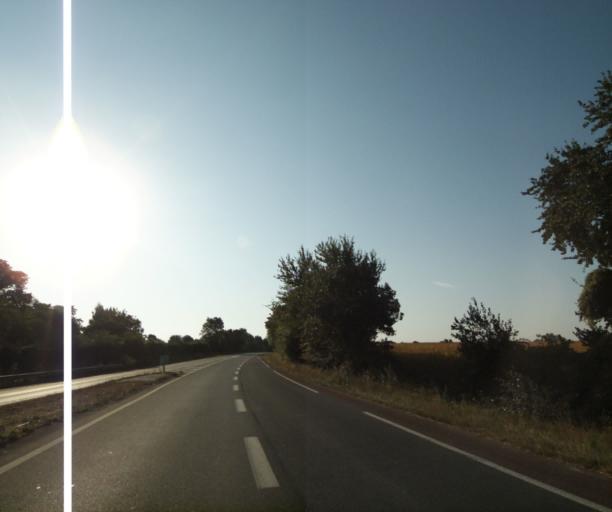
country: FR
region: Poitou-Charentes
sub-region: Departement de la Charente-Maritime
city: Tonnay-Charente
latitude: 45.9512
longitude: -0.8705
